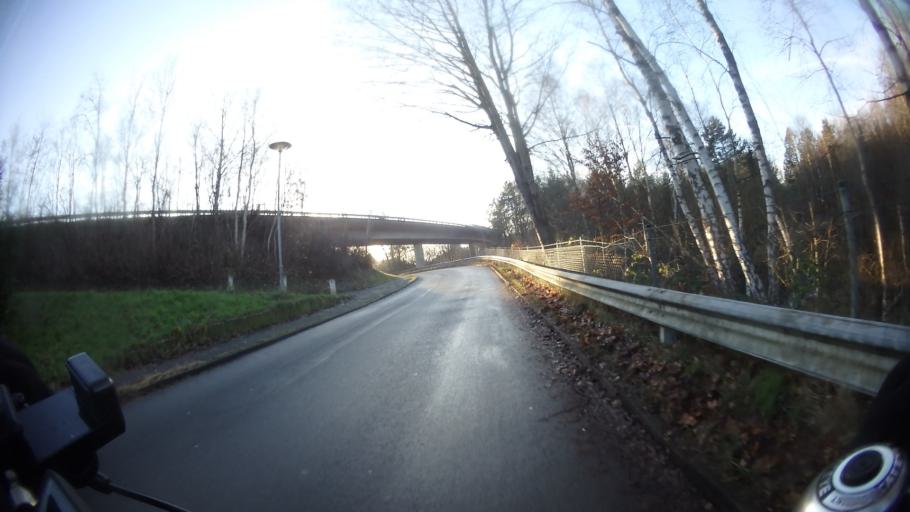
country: DE
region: Schleswig-Holstein
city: Ratekau
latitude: 53.9100
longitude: 10.7844
